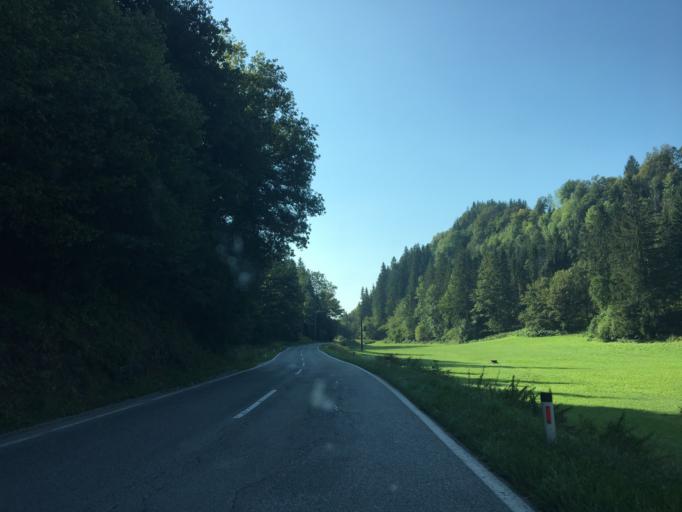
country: AT
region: Carinthia
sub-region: Politischer Bezirk Sankt Veit an der Glan
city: Bruckl
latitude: 46.7145
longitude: 14.5621
